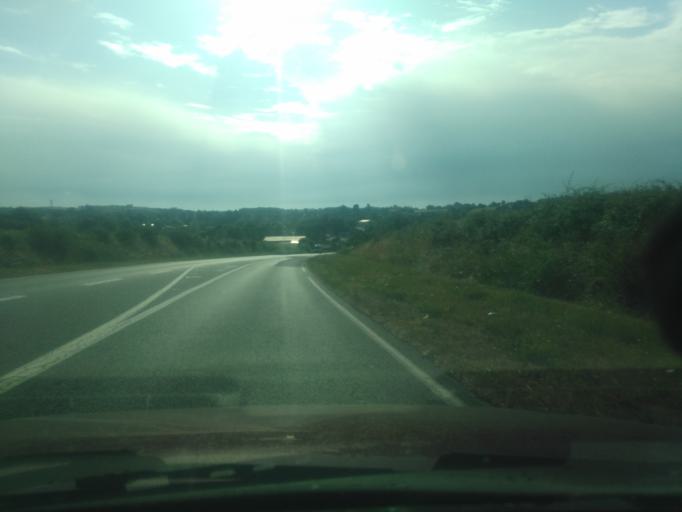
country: FR
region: Pays de la Loire
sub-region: Departement de la Vendee
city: La Tardiere
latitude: 46.6527
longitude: -0.6967
